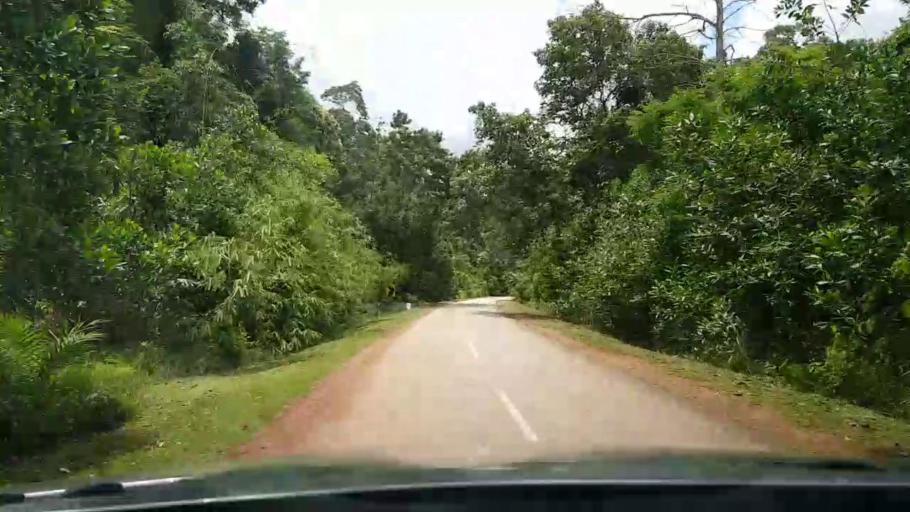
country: MY
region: Pahang
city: Pekan
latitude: 3.1413
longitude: 102.9716
